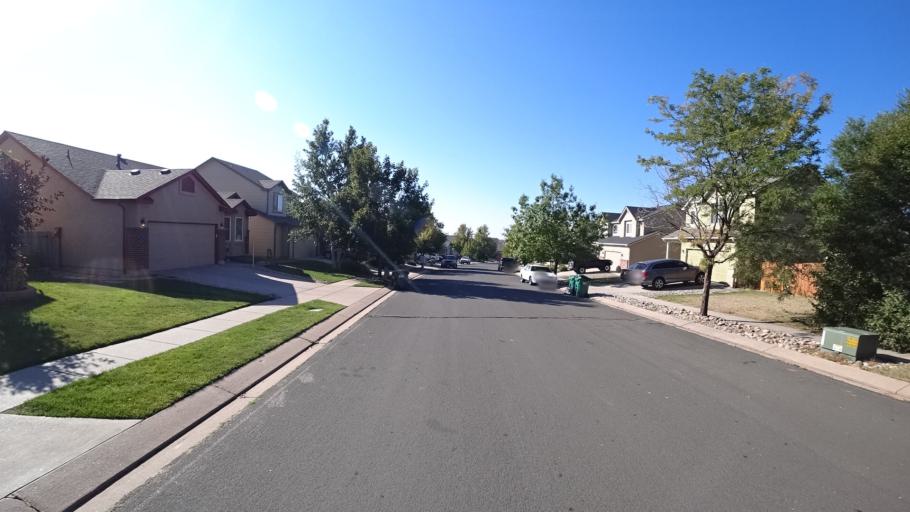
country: US
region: Colorado
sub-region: El Paso County
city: Cimarron Hills
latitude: 38.8907
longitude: -104.6966
